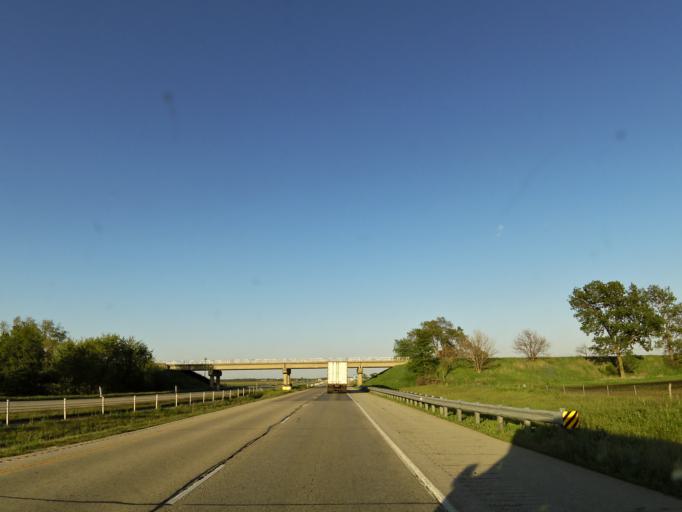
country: US
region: Illinois
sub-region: Vermilion County
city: Oakwood
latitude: 40.1253
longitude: -87.8132
